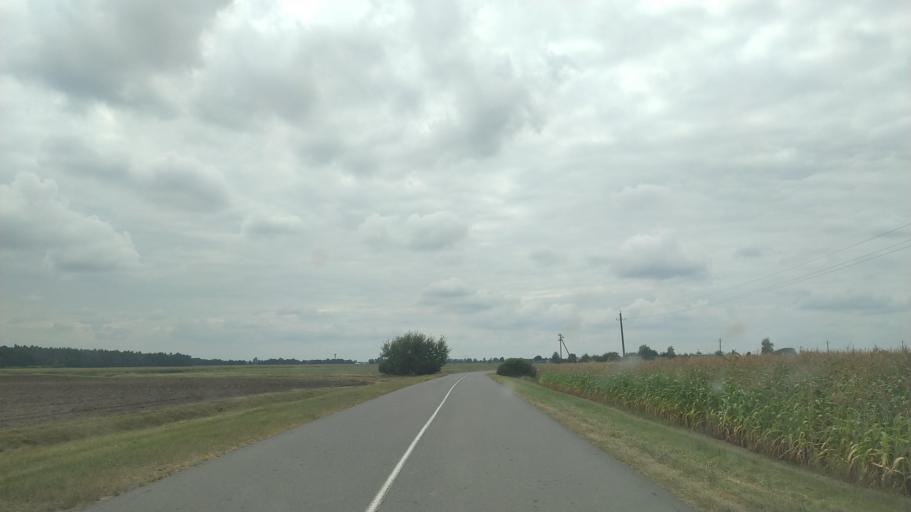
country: BY
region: Brest
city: Byelaazyorsk
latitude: 52.5399
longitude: 25.1249
